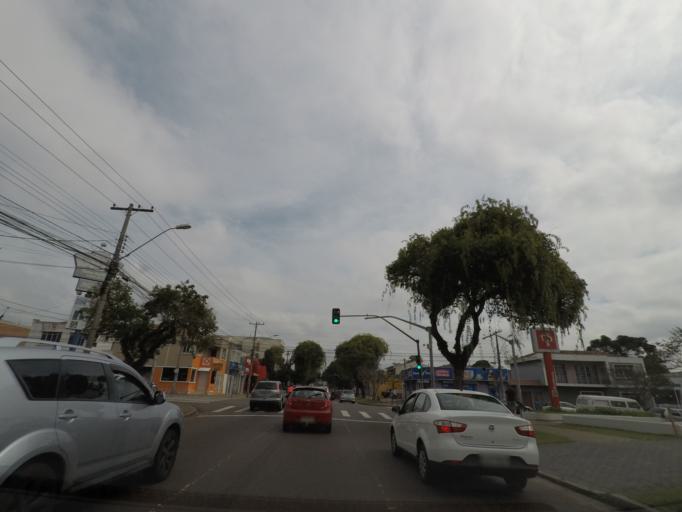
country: BR
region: Parana
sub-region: Curitiba
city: Curitiba
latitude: -25.4511
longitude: -49.2667
